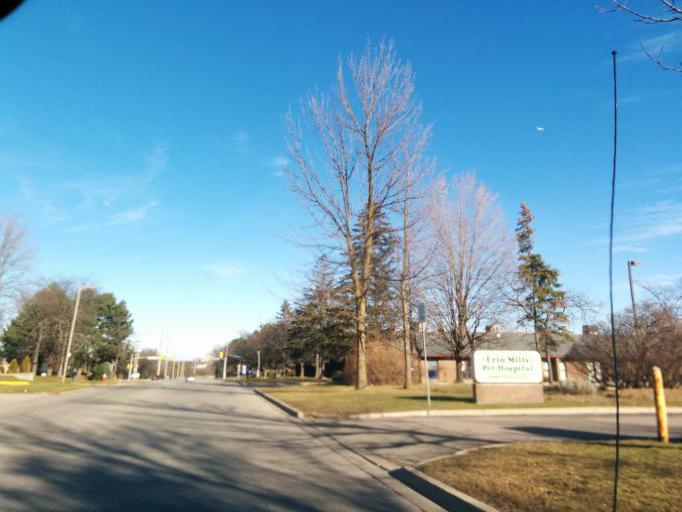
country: CA
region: Ontario
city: Mississauga
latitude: 43.5320
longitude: -79.6785
